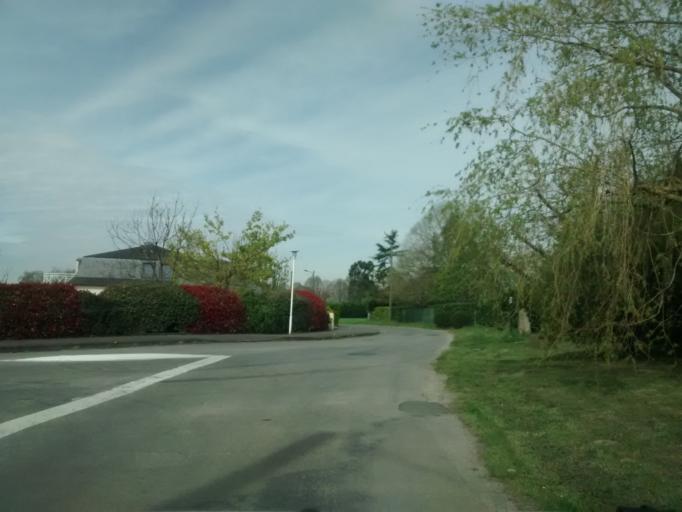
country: FR
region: Brittany
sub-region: Departement d'Ille-et-Vilaine
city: Noyal-sur-Vilaine
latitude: 48.1229
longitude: -1.5230
